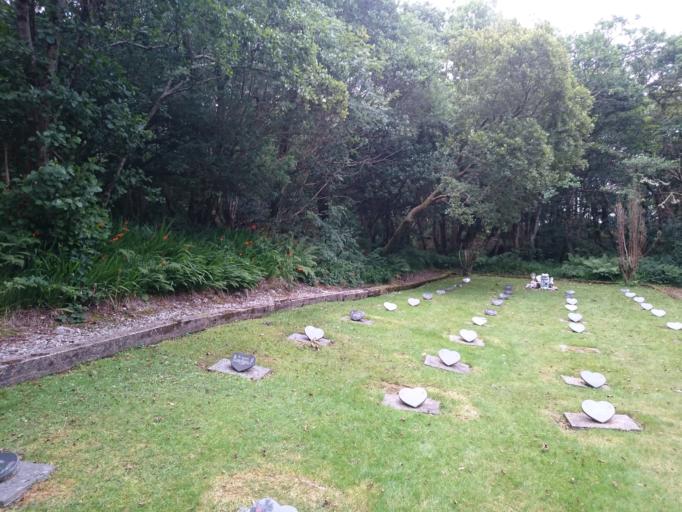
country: IE
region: Connaught
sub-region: County Galway
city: Clifden
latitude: 53.5523
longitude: -9.9447
